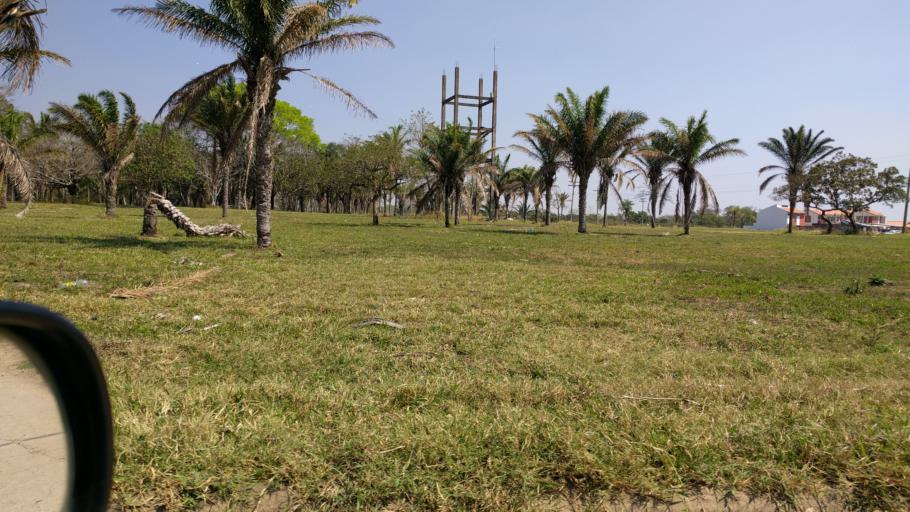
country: BO
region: Santa Cruz
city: Santa Cruz de la Sierra
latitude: -17.7538
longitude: -63.2302
